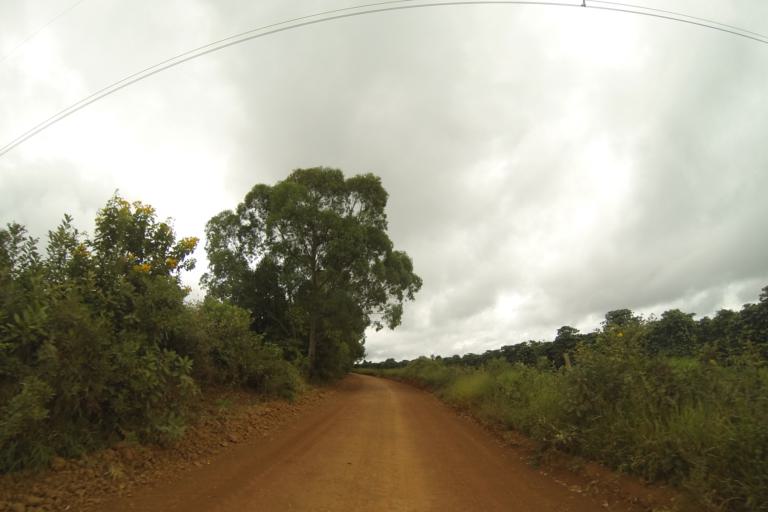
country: BR
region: Minas Gerais
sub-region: Campos Altos
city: Campos Altos
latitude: -19.8652
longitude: -46.3065
